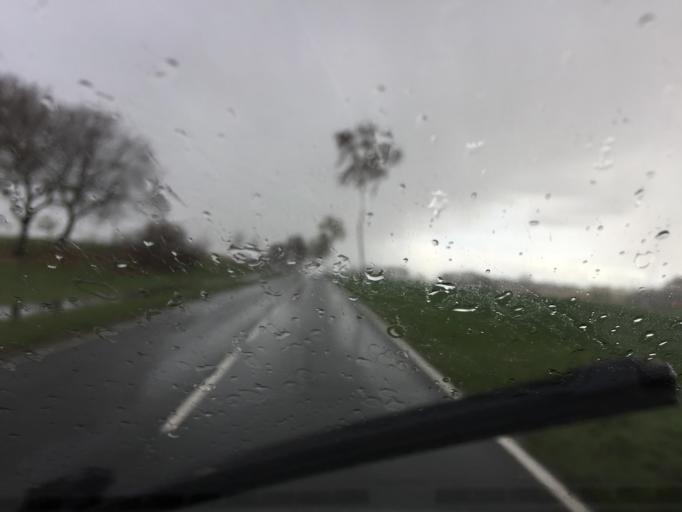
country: DE
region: Lower Saxony
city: Syke
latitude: 52.9285
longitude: 8.8833
